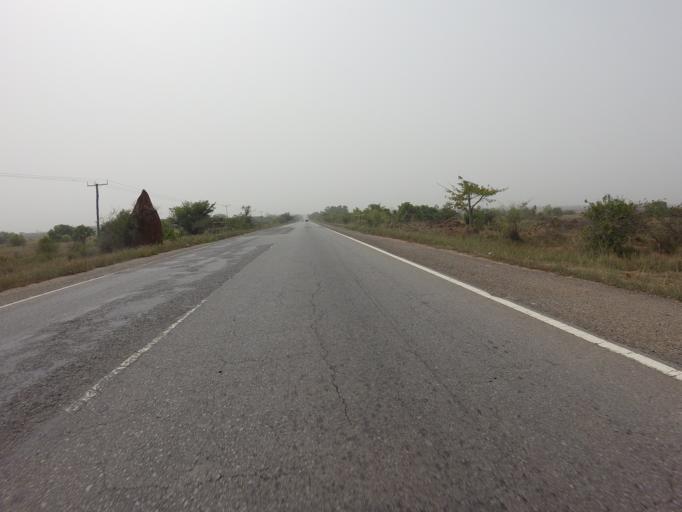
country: GH
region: Volta
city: Anloga
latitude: 5.9614
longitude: 0.5243
